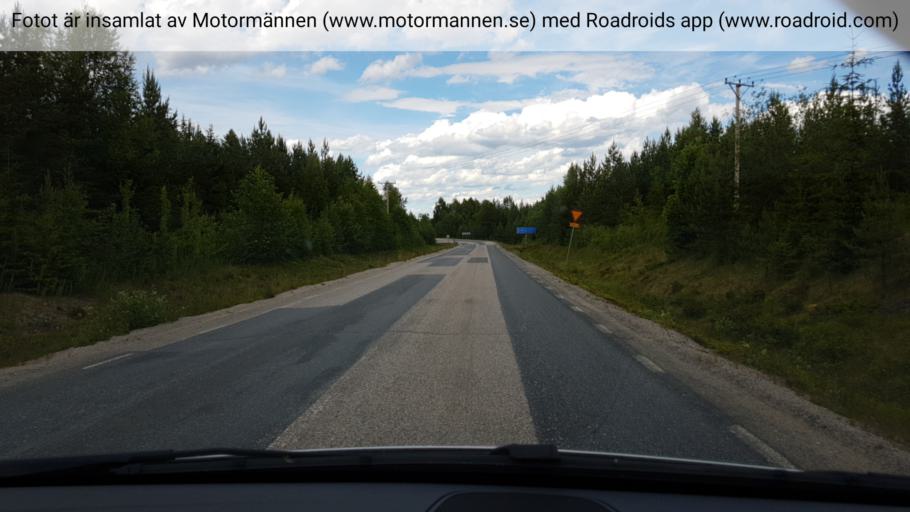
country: SE
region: Jaemtland
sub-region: Braecke Kommun
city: Braecke
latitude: 62.3934
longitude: 15.2302
